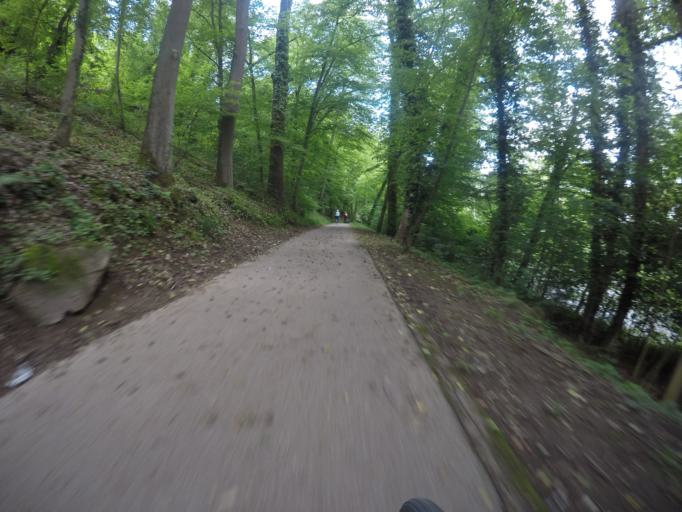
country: DE
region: Baden-Wuerttemberg
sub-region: Karlsruhe Region
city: Pforzheim
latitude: 48.8745
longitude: 8.6753
